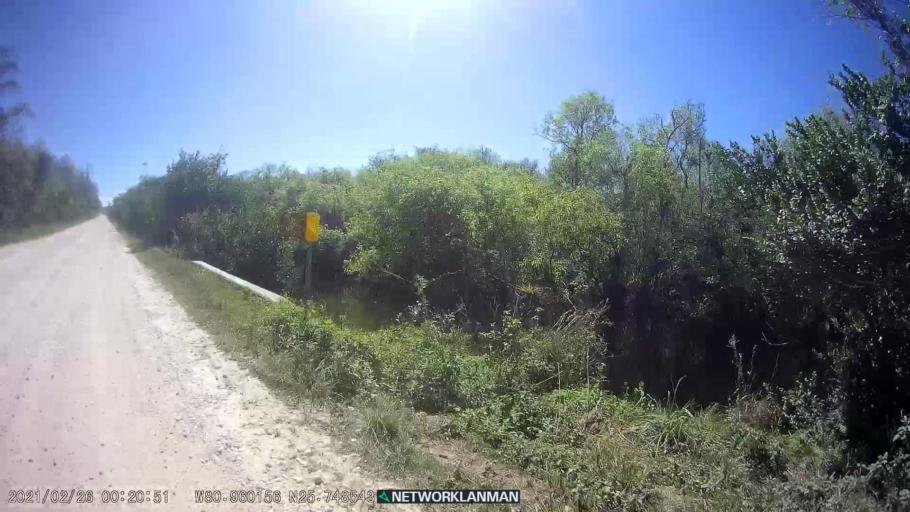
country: US
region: Florida
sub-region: Miami-Dade County
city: The Hammocks
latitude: 25.7485
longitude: -80.9601
